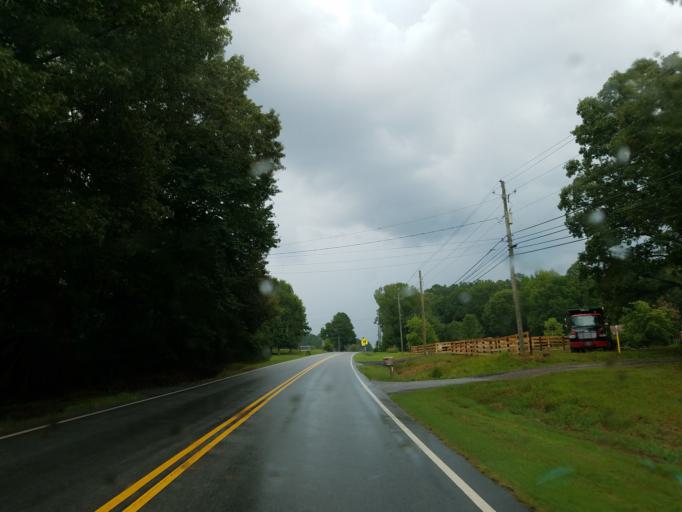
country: US
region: Georgia
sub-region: Floyd County
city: Shannon
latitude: 34.3862
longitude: -85.1706
